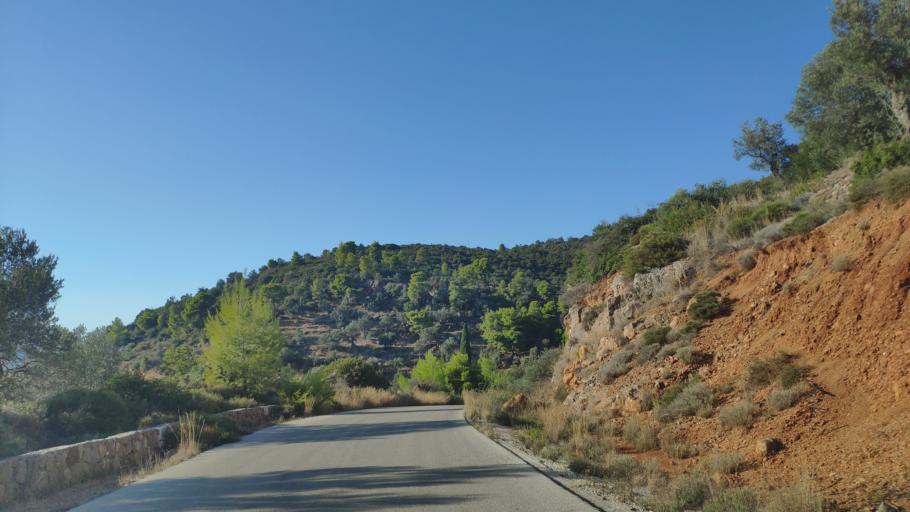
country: GR
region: Attica
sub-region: Nomos Piraios
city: Galatas
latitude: 37.5776
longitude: 23.3587
